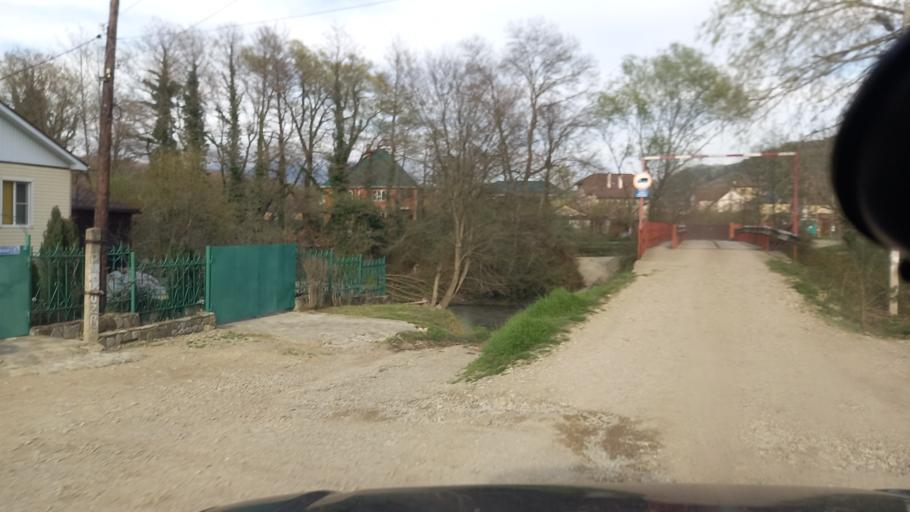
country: RU
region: Krasnodarskiy
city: Arkhipo-Osipovka
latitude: 44.3682
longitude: 38.5440
